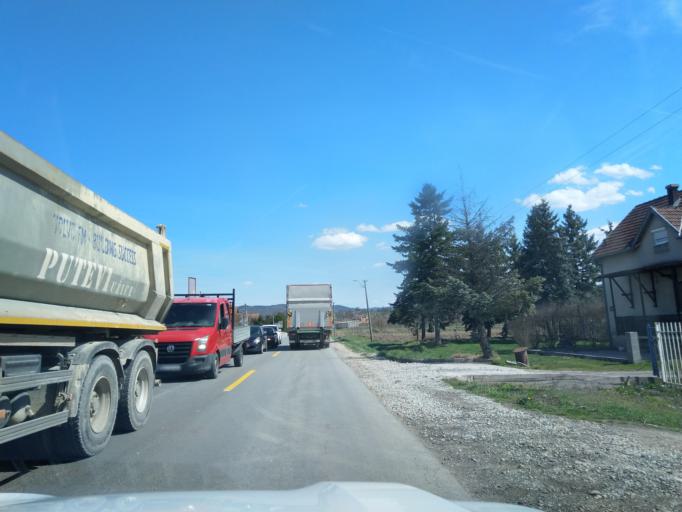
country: RS
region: Central Serbia
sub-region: Zlatiborski Okrug
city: Pozega
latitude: 43.8303
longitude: 20.0585
